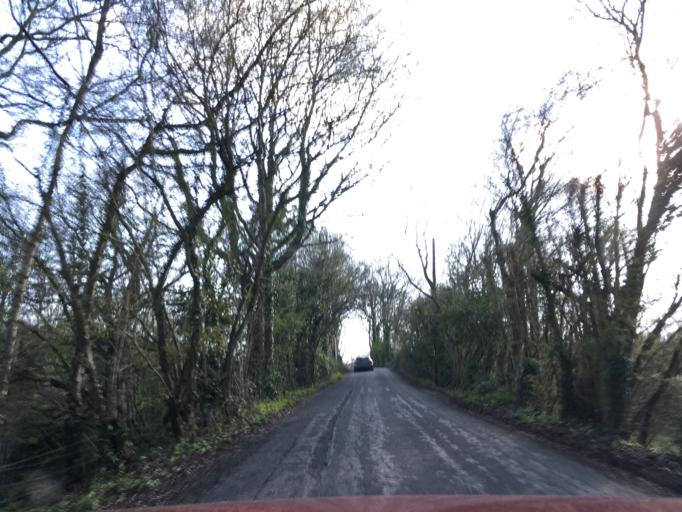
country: GB
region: Wales
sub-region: Torfaen County Borough
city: New Inn
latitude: 51.7148
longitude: -2.9608
